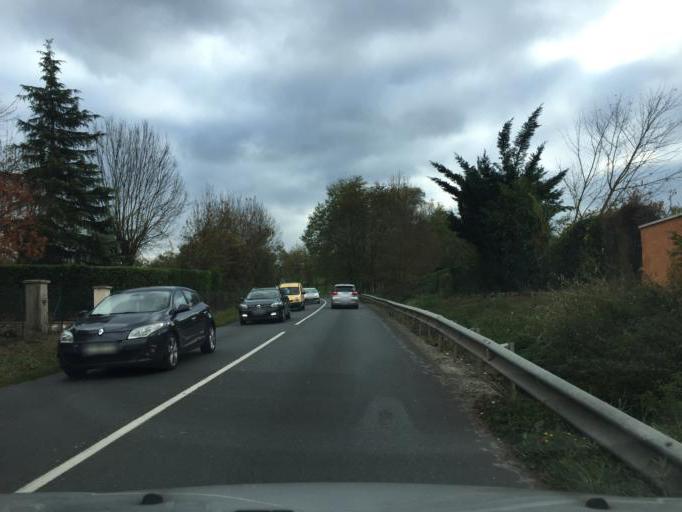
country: FR
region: Rhone-Alpes
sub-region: Departement de l'Ain
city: Jassans-Riottier
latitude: 45.9859
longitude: 4.7660
